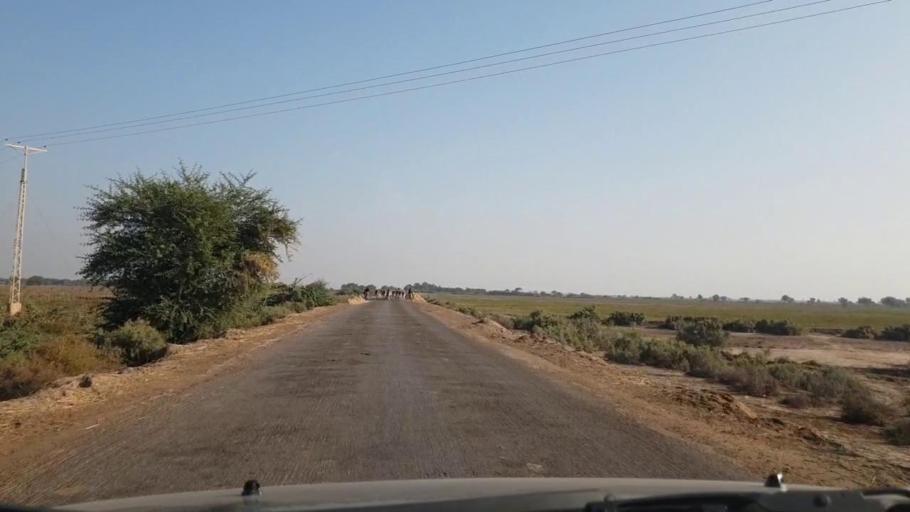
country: PK
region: Sindh
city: Tando Bago
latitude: 24.8562
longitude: 69.0421
